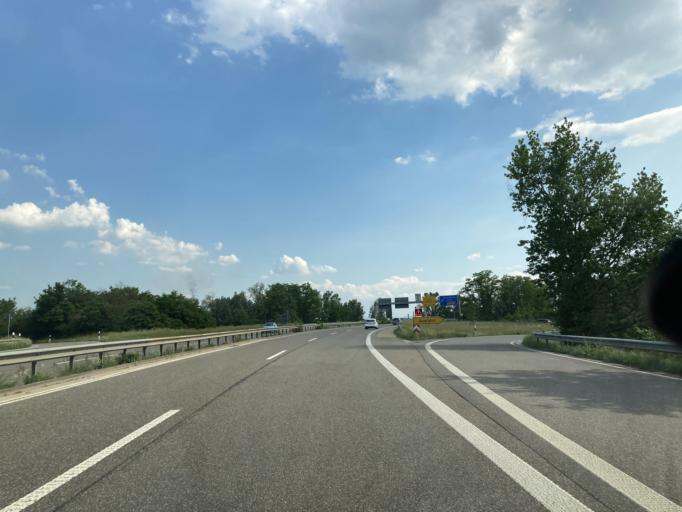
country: DE
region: Rheinland-Pfalz
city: Worth am Rhein
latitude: 49.0465
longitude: 8.2772
